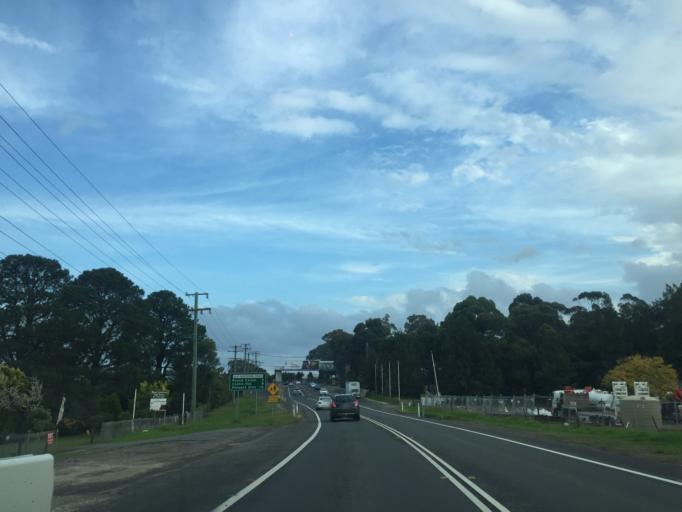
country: AU
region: New South Wales
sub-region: The Hills Shire
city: Glenhaven
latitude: -33.6845
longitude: 151.0276
